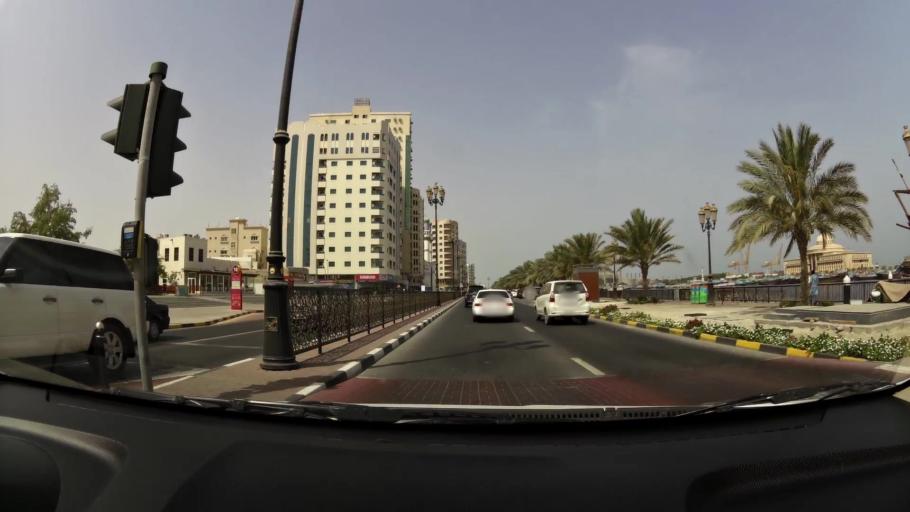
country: AE
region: Ash Shariqah
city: Sharjah
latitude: 25.3595
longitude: 55.3830
